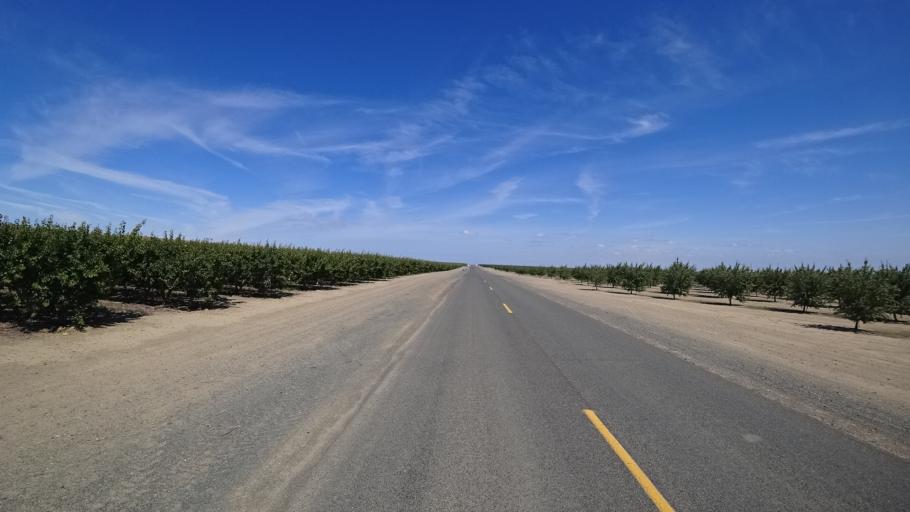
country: US
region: California
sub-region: Kings County
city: Kettleman City
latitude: 35.9403
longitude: -119.9275
